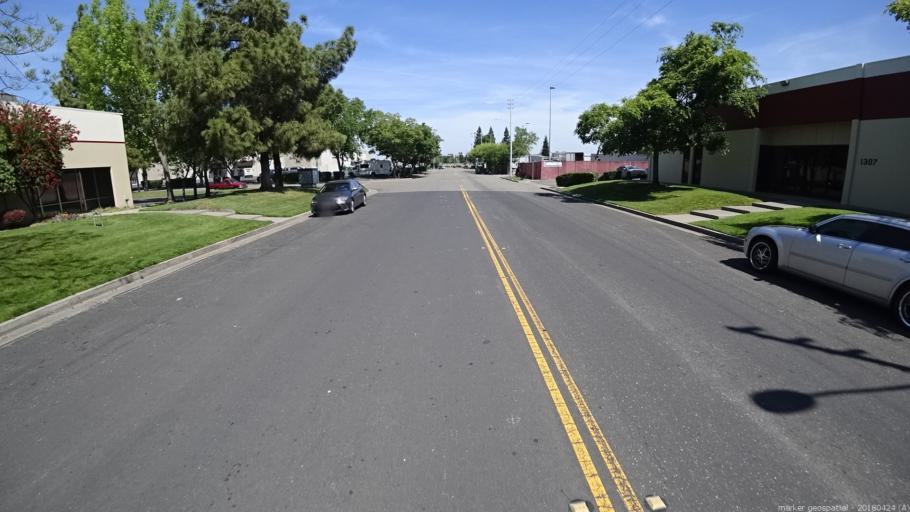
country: US
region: California
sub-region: Yolo County
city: West Sacramento
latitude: 38.5722
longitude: -121.5414
